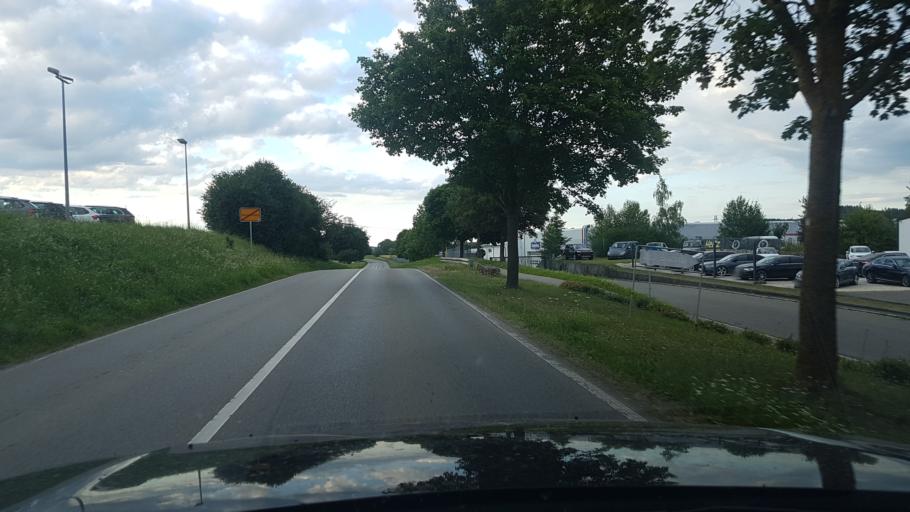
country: DE
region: Baden-Wuerttemberg
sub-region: Freiburg Region
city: Donaueschingen
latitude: 47.9645
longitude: 8.5055
